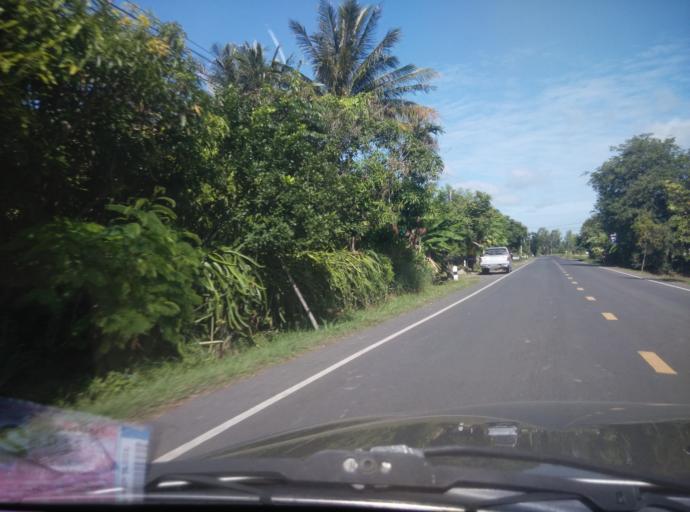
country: TH
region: Sisaket
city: Uthumphon Phisai
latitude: 15.1194
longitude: 104.2225
